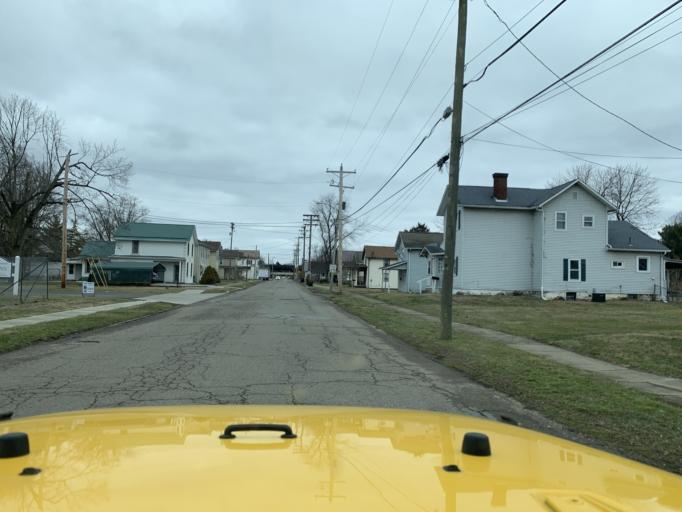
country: US
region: Ohio
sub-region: Licking County
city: Newark
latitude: 40.0507
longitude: -82.4066
